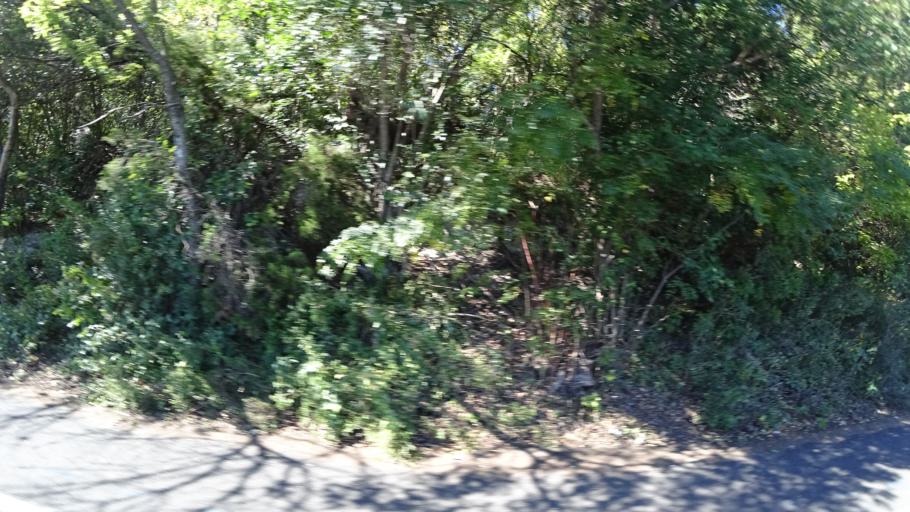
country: US
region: Texas
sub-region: Travis County
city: Rollingwood
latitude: 30.2309
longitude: -97.7772
